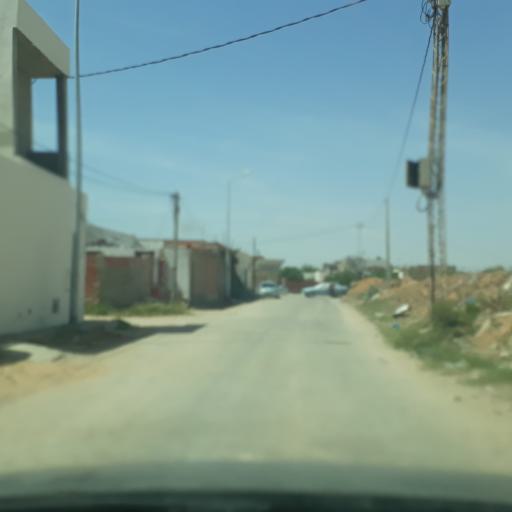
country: TN
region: Safaqis
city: Al Qarmadah
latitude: 34.8280
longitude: 10.7798
